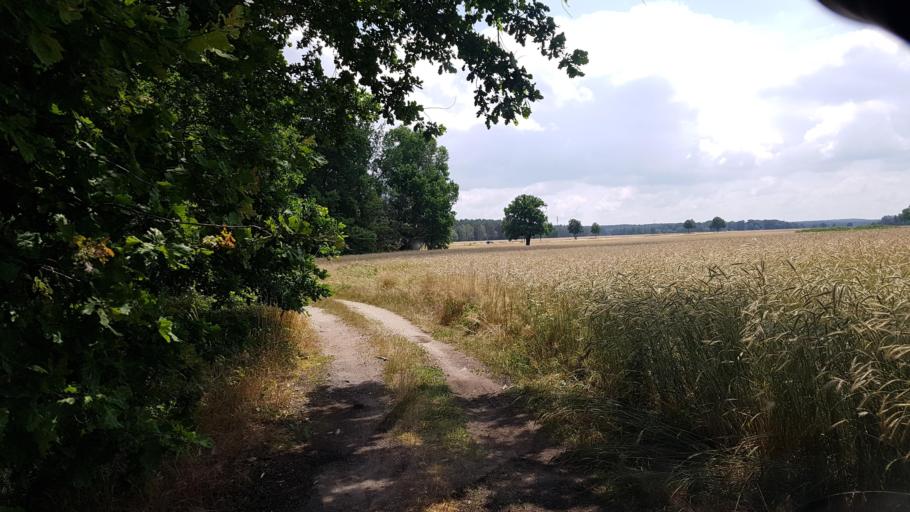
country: DE
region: Brandenburg
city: Crinitz
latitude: 51.7534
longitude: 13.8549
